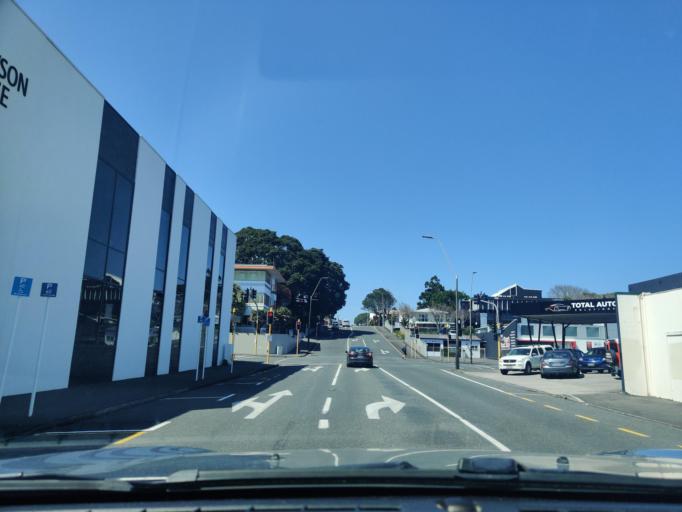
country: NZ
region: Taranaki
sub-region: New Plymouth District
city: New Plymouth
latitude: -39.0590
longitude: 174.0681
